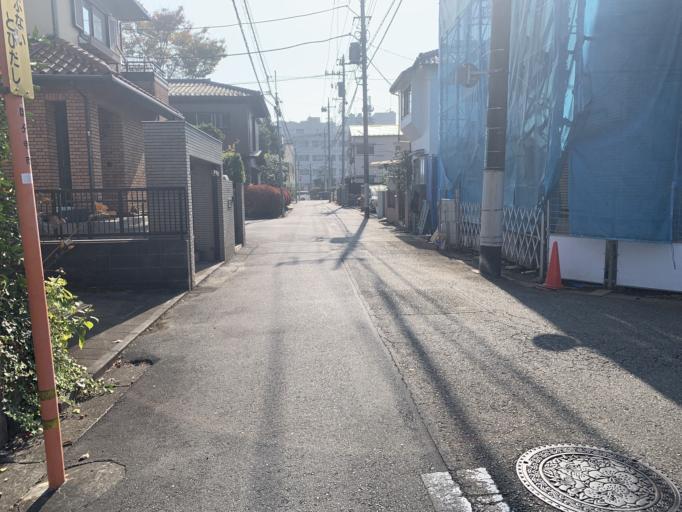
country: JP
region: Tokyo
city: Kokubunji
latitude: 35.6974
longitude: 139.4746
